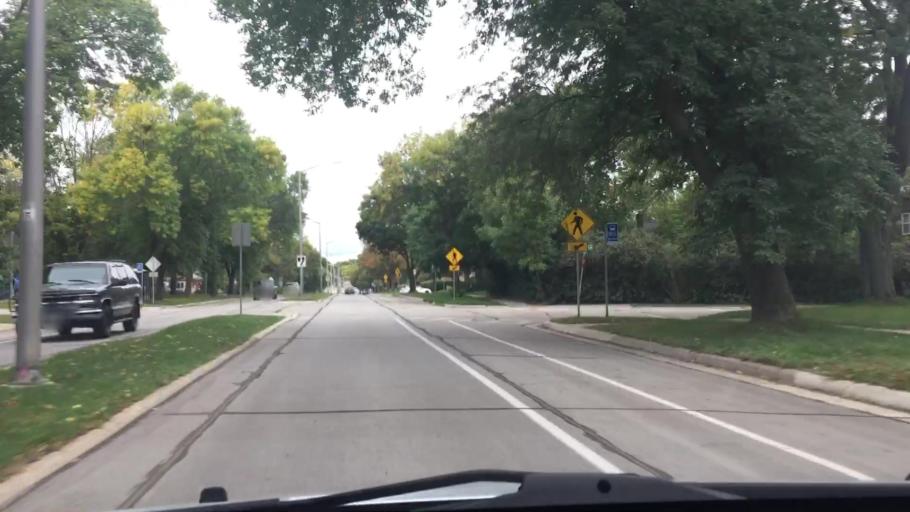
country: US
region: Wisconsin
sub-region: Waukesha County
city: Waukesha
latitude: 42.9938
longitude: -88.2322
